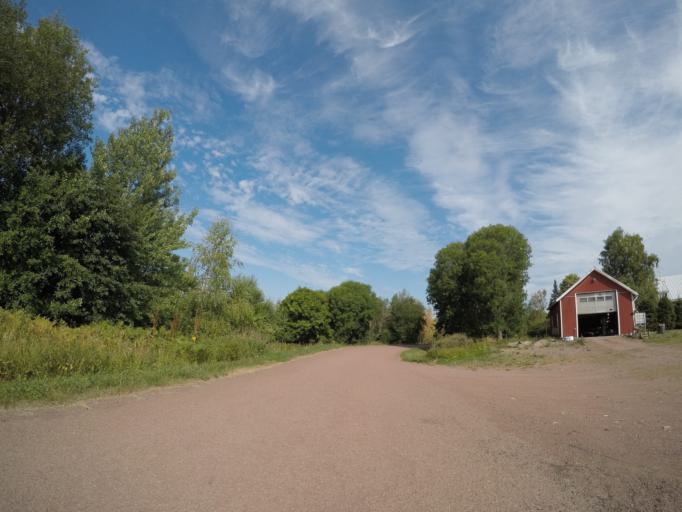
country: AX
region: Alands landsbygd
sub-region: Finstroem
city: Finstroem
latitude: 60.2056
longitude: 19.8742
